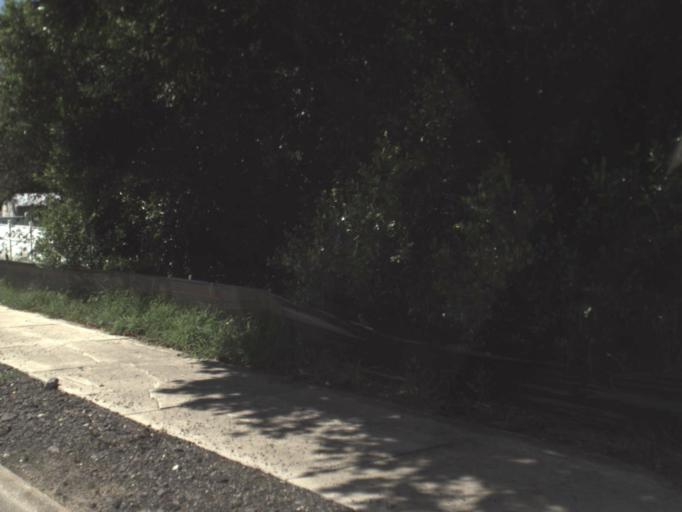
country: US
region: Florida
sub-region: Polk County
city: Haines City
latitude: 28.0954
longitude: -81.6233
